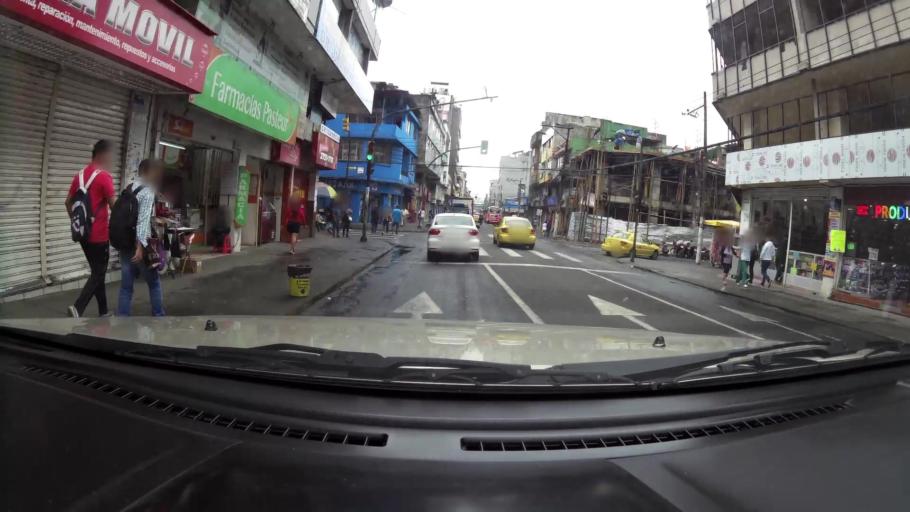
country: EC
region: Santo Domingo de los Tsachilas
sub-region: Canton Santo Domingo de los Colorados
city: Santo Domingo de los Colorados
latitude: -0.2538
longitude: -79.1706
